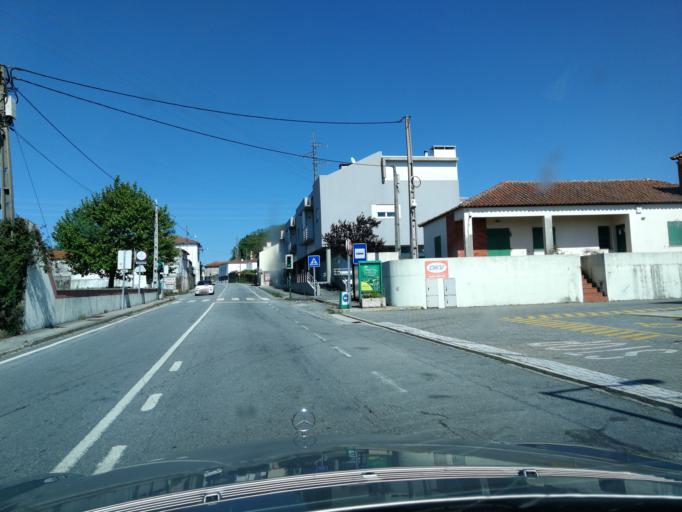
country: PT
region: Viana do Castelo
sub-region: Viana do Castelo
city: Meadela
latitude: 41.7072
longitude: -8.7824
